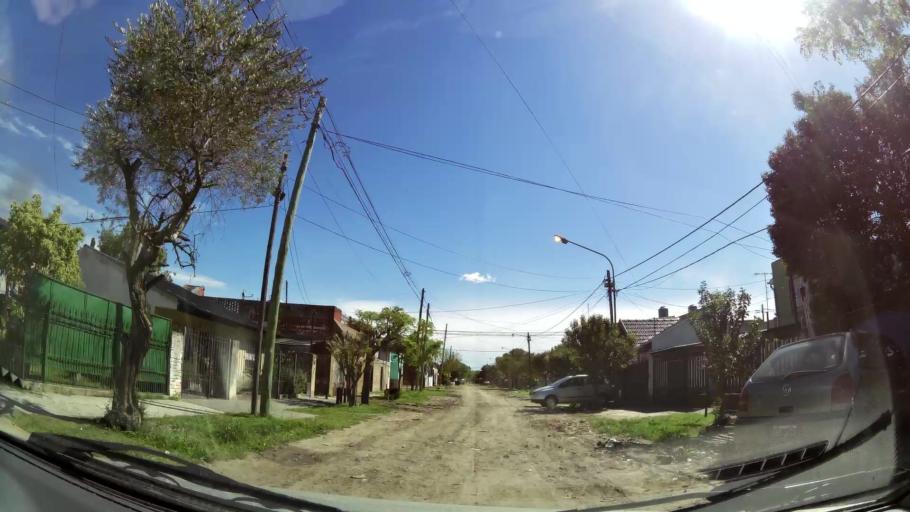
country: AR
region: Buenos Aires
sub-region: Partido de Almirante Brown
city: Adrogue
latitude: -34.7828
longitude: -58.3466
